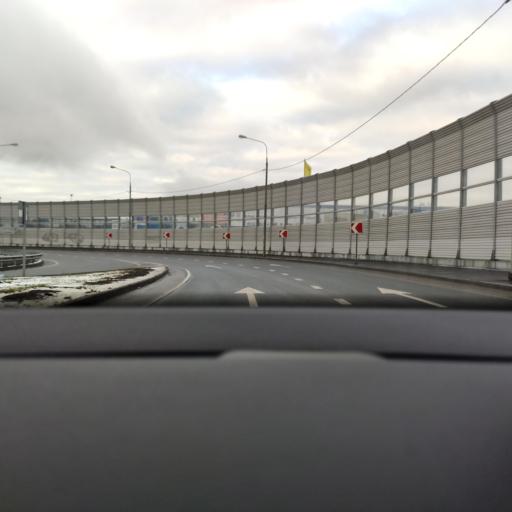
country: RU
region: Moskovskaya
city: Lesnyye Polyany
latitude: 55.9635
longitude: 37.8435
